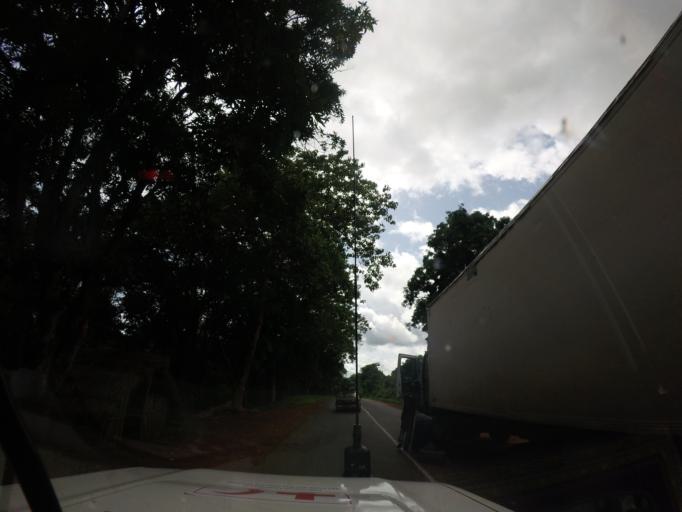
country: GN
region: Mamou
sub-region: Mamou Prefecture
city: Mamou
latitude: 10.3099
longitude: -12.0090
